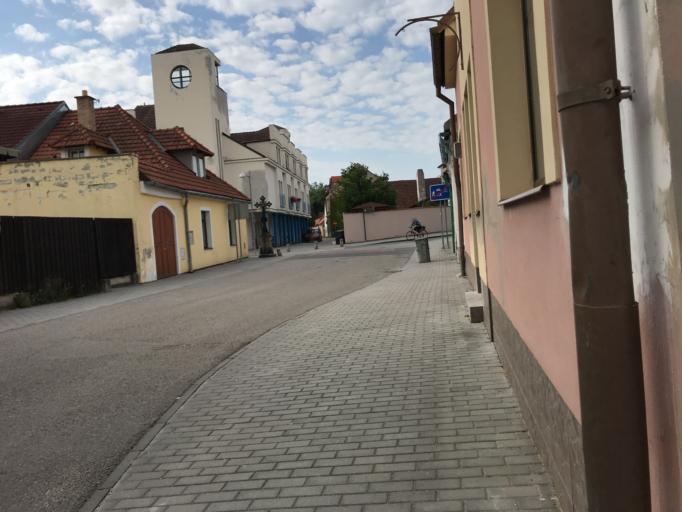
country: CZ
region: Jihocesky
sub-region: Okres Jindrichuv Hradec
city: Trebon
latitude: 49.0044
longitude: 14.7652
